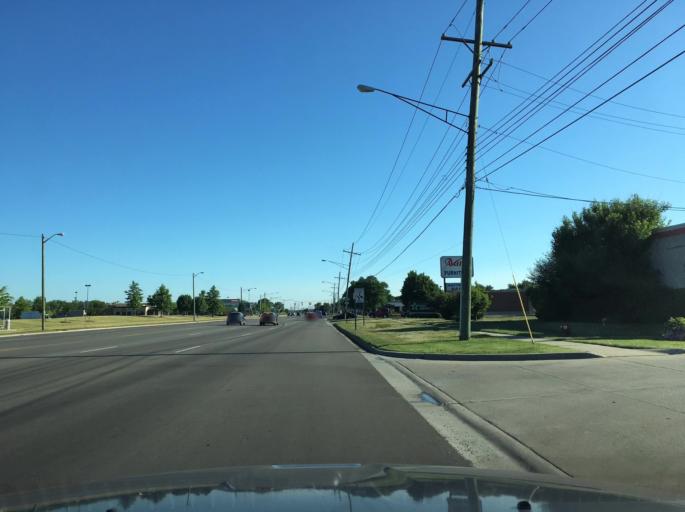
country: US
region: Michigan
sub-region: Macomb County
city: Sterling Heights
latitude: 42.5388
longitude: -83.0290
